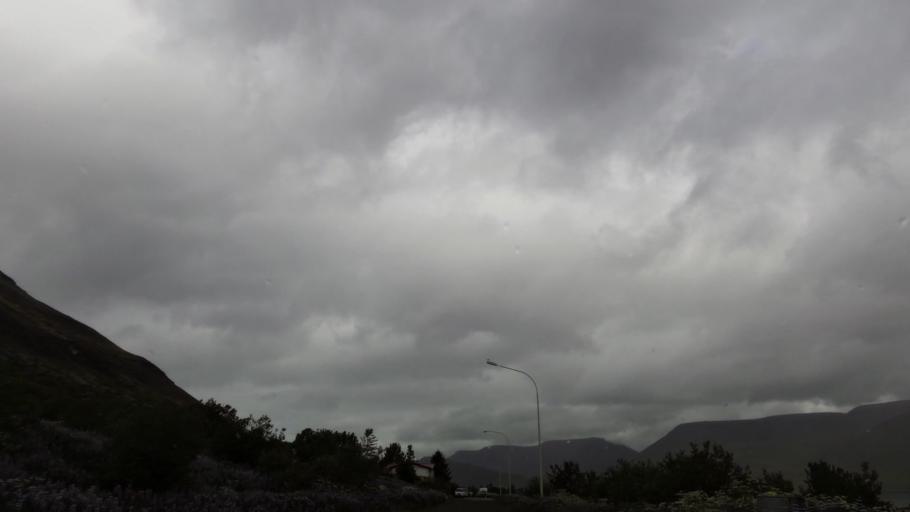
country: IS
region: Westfjords
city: Isafjoerdur
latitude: 65.8745
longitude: -23.4901
